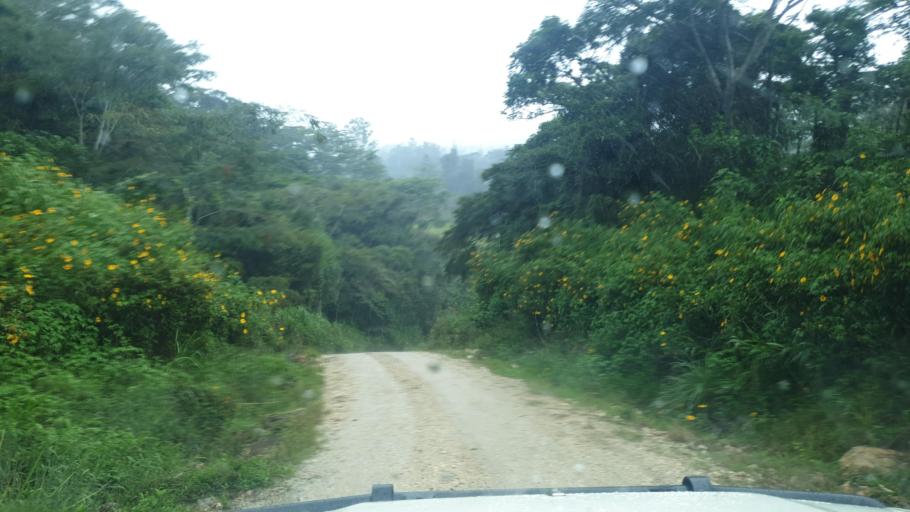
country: PG
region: Eastern Highlands
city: Goroka
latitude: -6.1972
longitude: 145.2122
